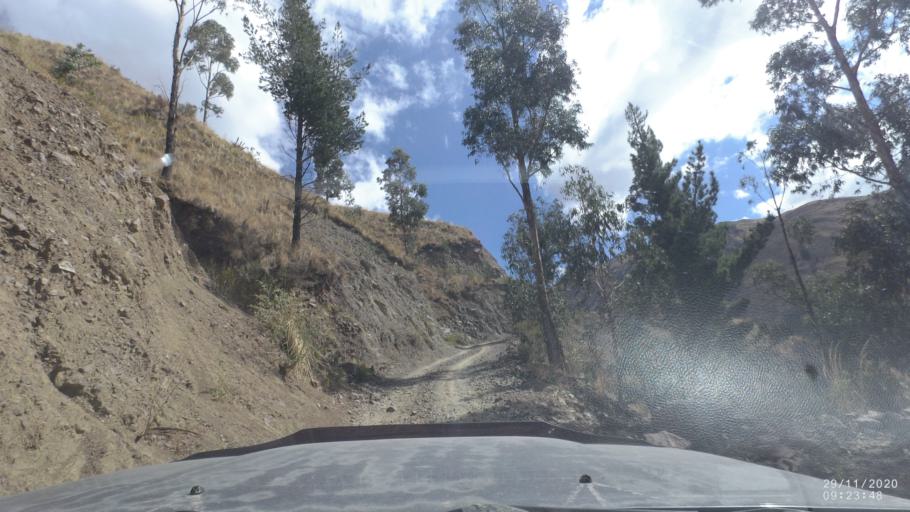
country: BO
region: Cochabamba
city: Cochabamba
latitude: -17.3206
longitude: -66.1855
